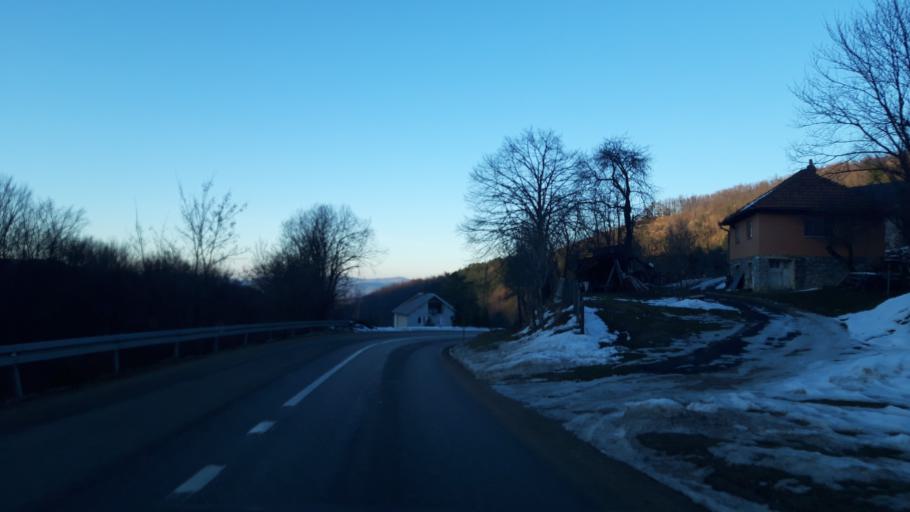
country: BA
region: Republika Srpska
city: Vlasenica
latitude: 44.1653
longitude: 18.9492
